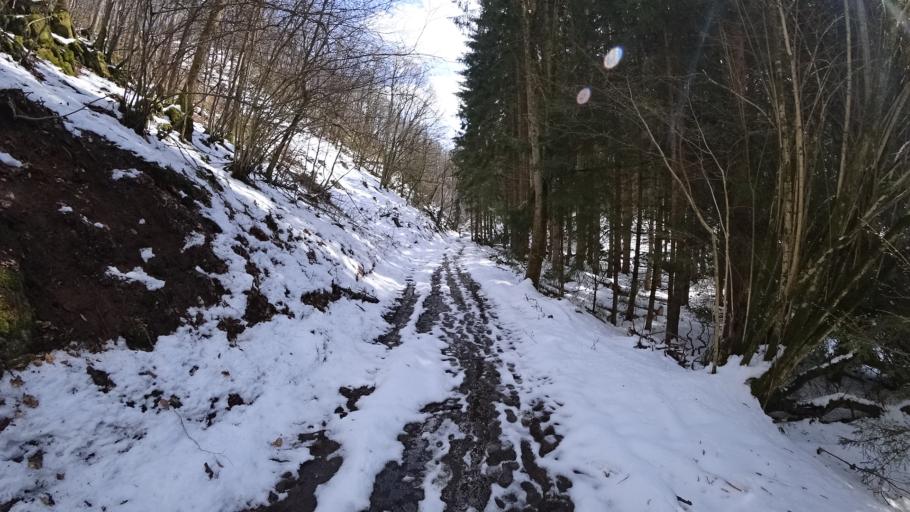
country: DE
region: Rheinland-Pfalz
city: Kausen
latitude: 50.7360
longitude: 7.8659
